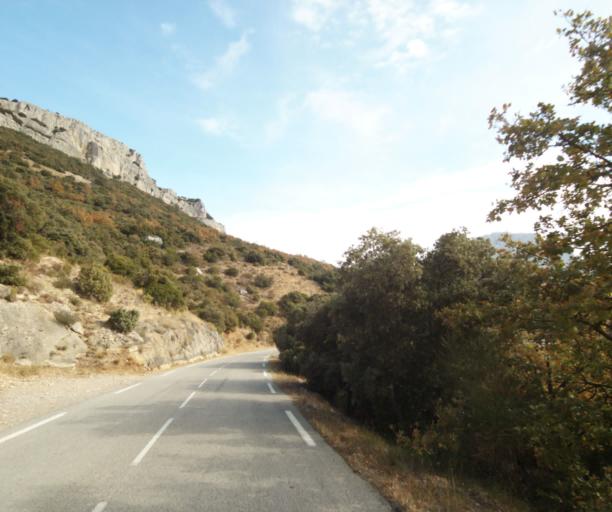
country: FR
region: Provence-Alpes-Cote d'Azur
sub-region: Departement des Bouches-du-Rhone
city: Gemenos
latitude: 43.3160
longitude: 5.6675
